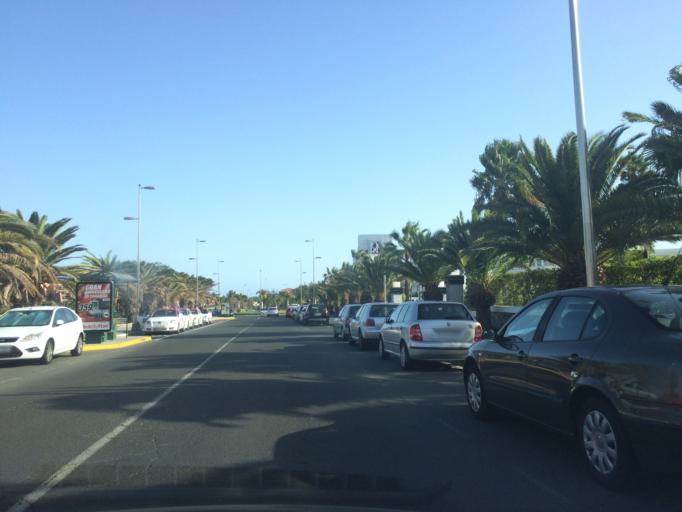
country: ES
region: Canary Islands
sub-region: Provincia de Las Palmas
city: Maspalomas
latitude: 27.7419
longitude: -15.6044
